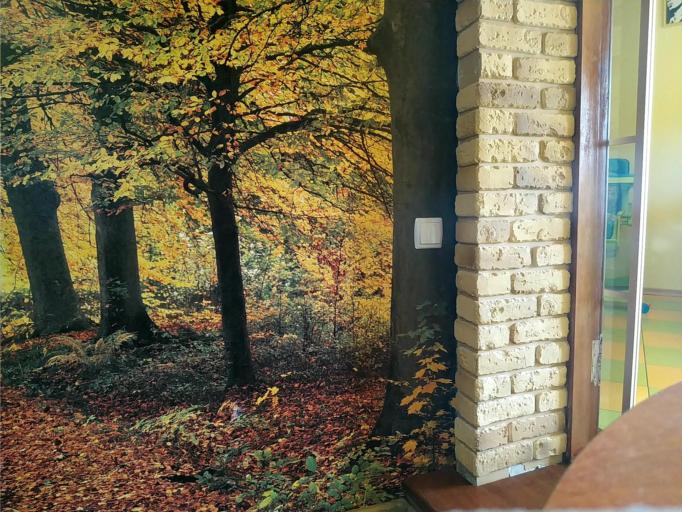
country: RU
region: Smolensk
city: Katyn'
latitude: 54.9522
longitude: 31.7105
